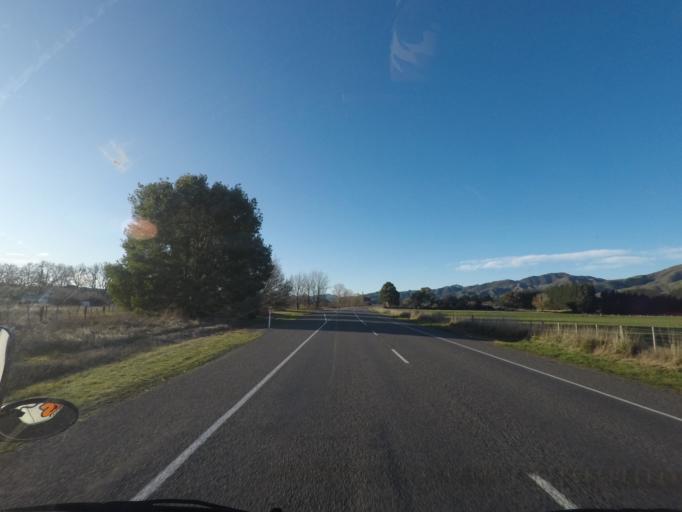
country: NZ
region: Canterbury
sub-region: Kaikoura District
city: Kaikoura
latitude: -42.7112
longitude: 173.2920
